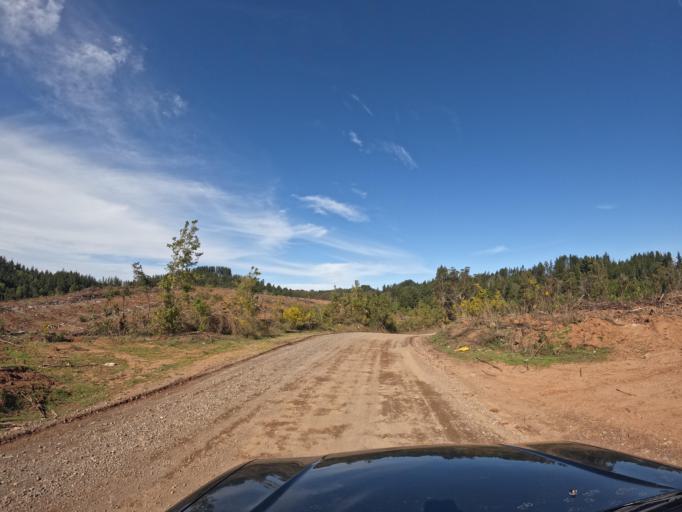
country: CL
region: Biobio
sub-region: Provincia de Biobio
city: La Laja
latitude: -37.0872
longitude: -72.8296
